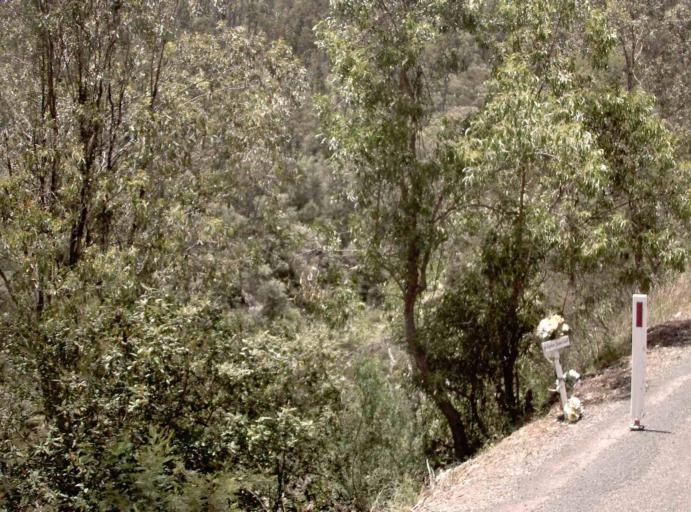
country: AU
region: Victoria
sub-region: East Gippsland
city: Bairnsdale
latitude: -37.4744
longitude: 147.8329
